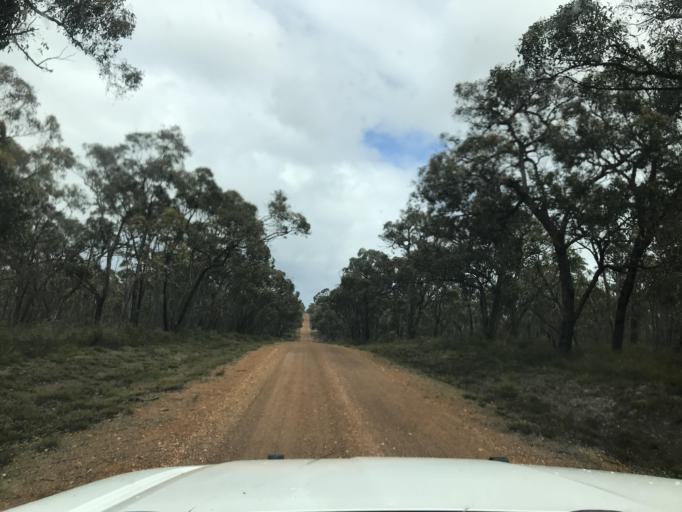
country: AU
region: South Australia
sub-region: Wattle Range
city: Penola
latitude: -37.2951
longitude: 141.3172
